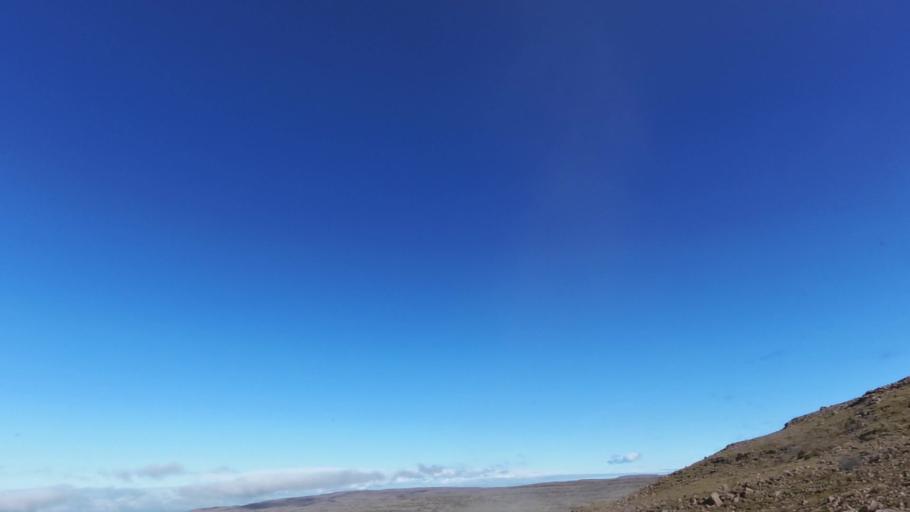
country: IS
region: West
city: Olafsvik
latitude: 65.5531
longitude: -24.2270
